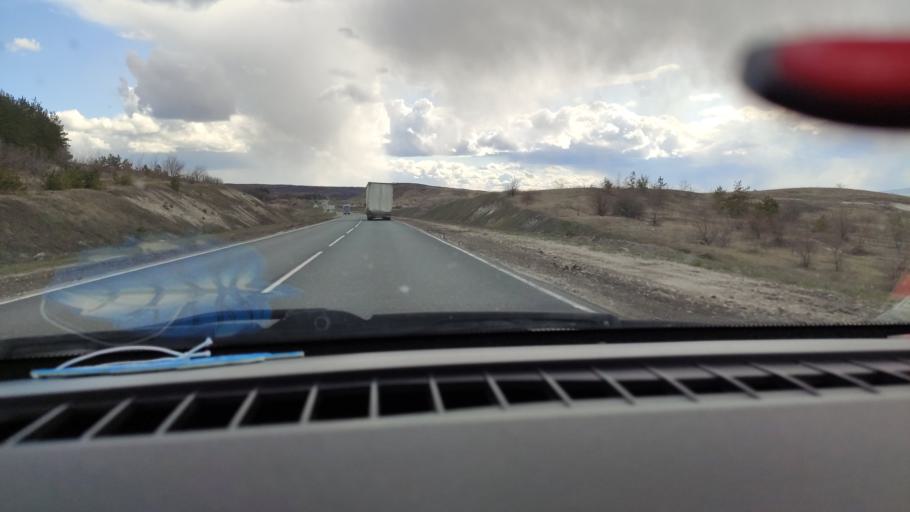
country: RU
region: Saratov
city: Alekseyevka
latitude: 52.3824
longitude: 47.9731
